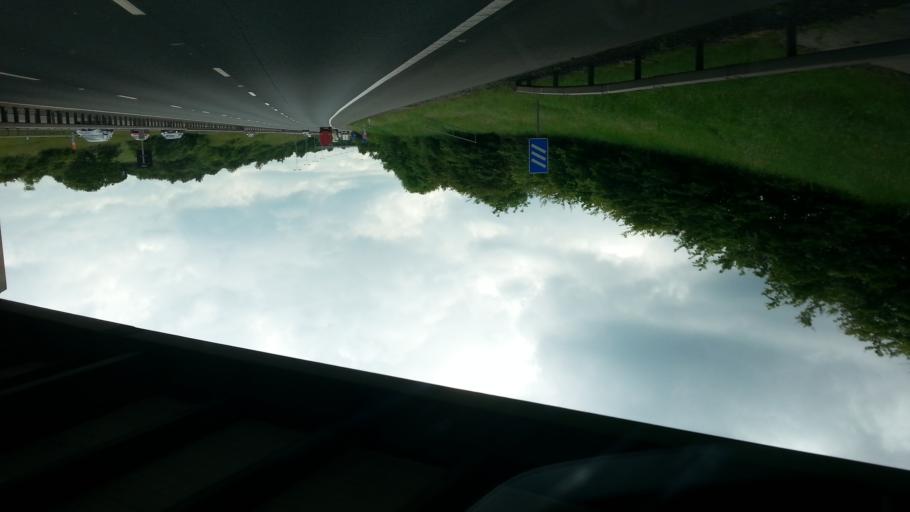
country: GB
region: England
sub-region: Staffordshire
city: Chasetown
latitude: 52.6599
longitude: -1.9135
